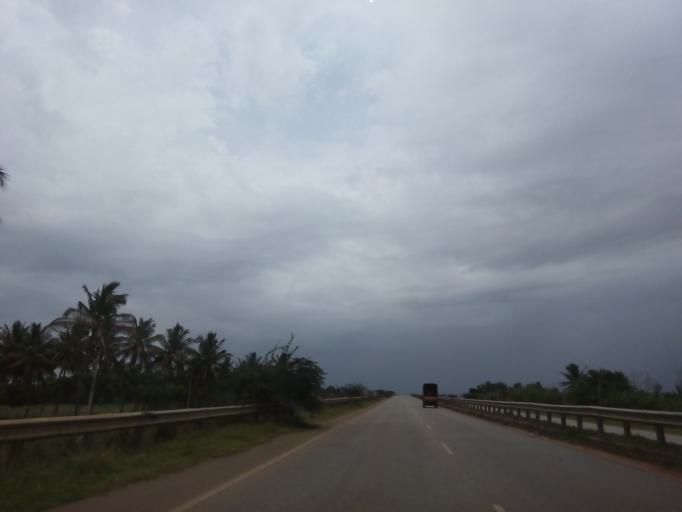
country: IN
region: Karnataka
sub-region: Davanagere
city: Harihar
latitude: 14.4846
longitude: 75.7987
